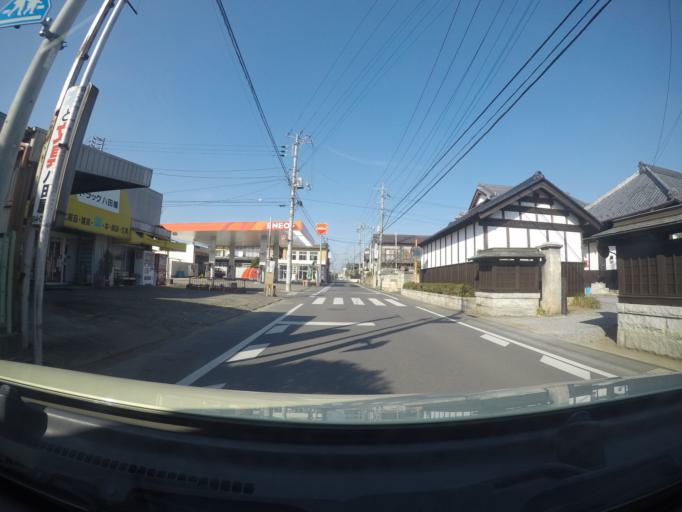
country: JP
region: Ibaraki
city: Tsukuba
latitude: 36.1373
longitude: 140.0905
